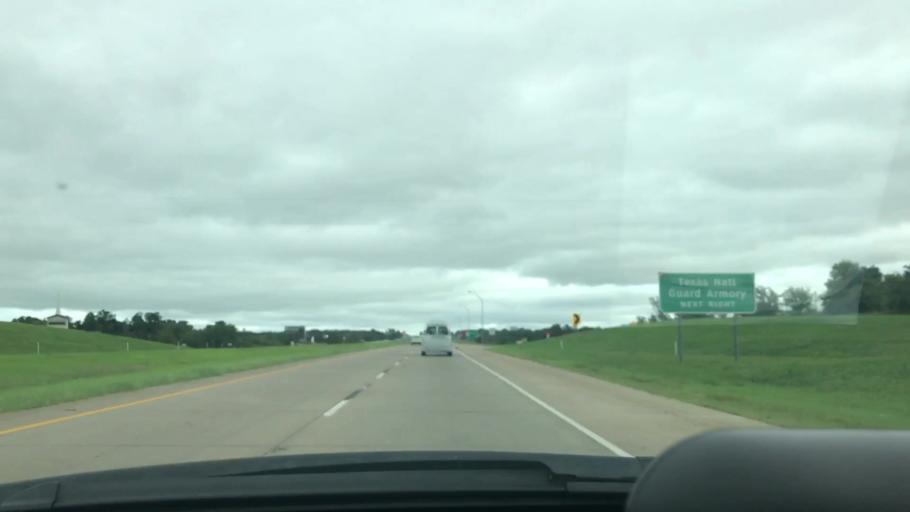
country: US
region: Texas
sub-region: Grayson County
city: Denison
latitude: 33.7222
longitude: -96.5852
